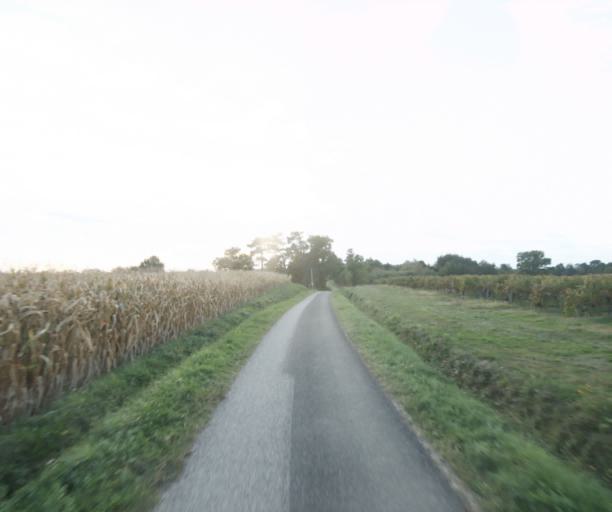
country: FR
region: Midi-Pyrenees
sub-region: Departement du Gers
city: Cazaubon
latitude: 43.8431
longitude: -0.0929
